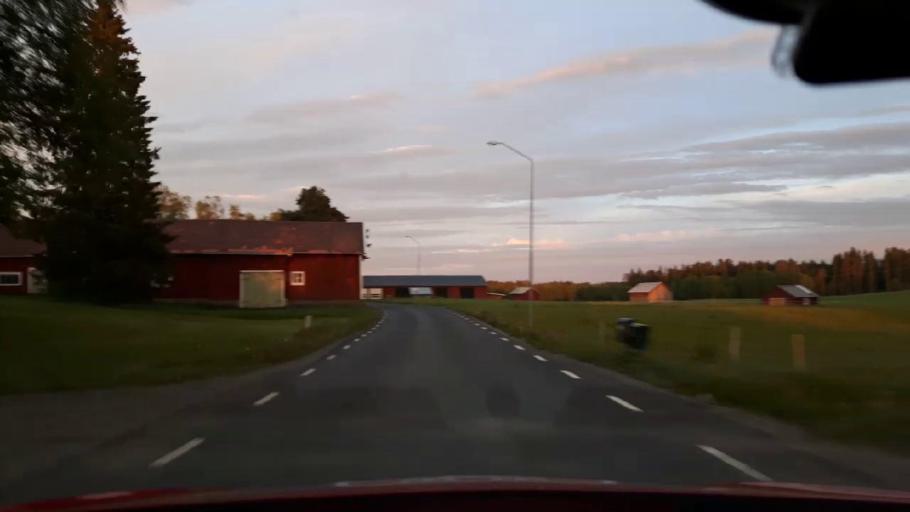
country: SE
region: Jaemtland
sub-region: OEstersunds Kommun
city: Brunflo
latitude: 63.0579
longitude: 14.8097
